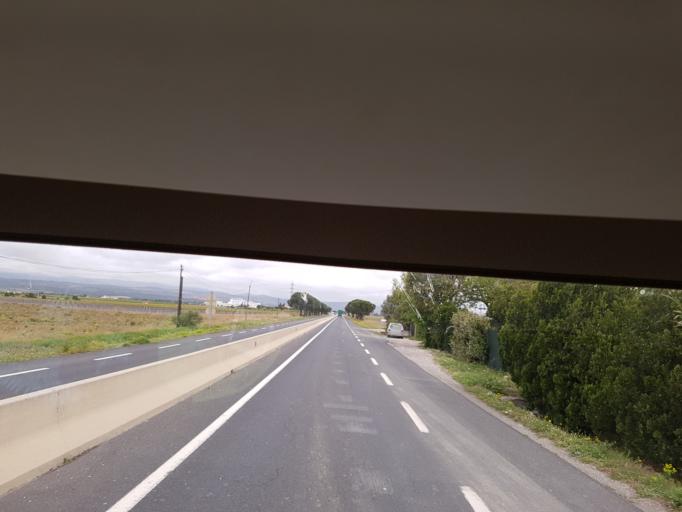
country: FR
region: Languedoc-Roussillon
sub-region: Departement des Pyrenees-Orientales
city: Salses-le-Chateau
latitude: 42.7929
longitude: 2.9077
